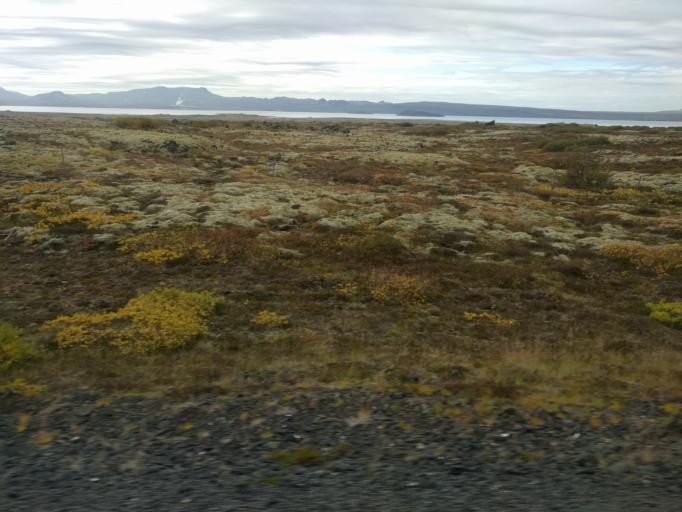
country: IS
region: South
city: Hveragerdi
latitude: 64.2042
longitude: -21.0382
